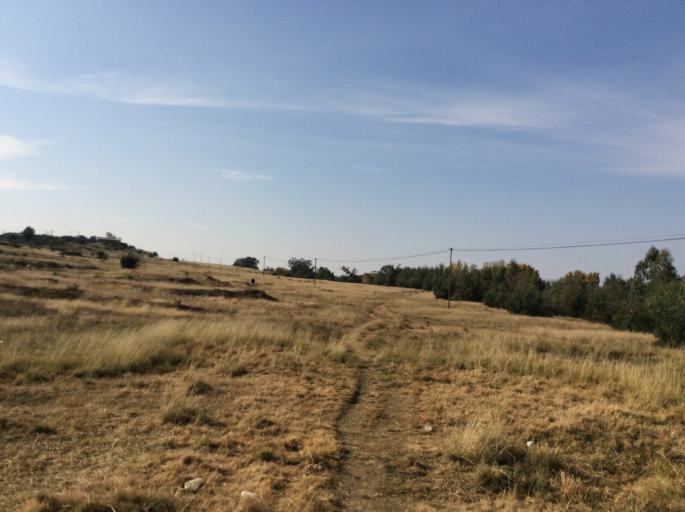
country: LS
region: Mafeteng
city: Mafeteng
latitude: -29.7245
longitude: 27.0253
